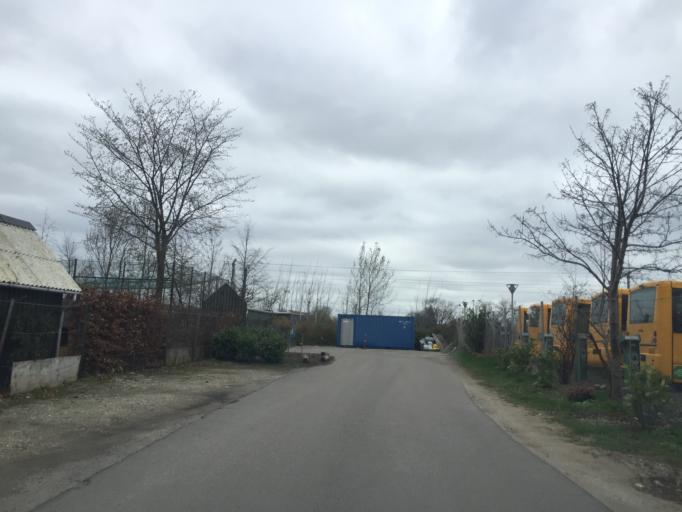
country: DK
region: Capital Region
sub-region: Kobenhavn
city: Copenhagen
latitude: 55.7164
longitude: 12.5637
